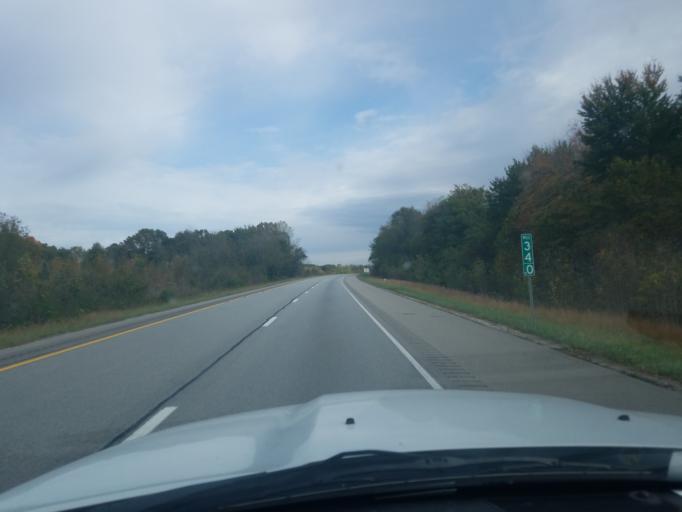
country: US
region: Indiana
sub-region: Warrick County
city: Chandler
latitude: 38.1830
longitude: -87.3898
